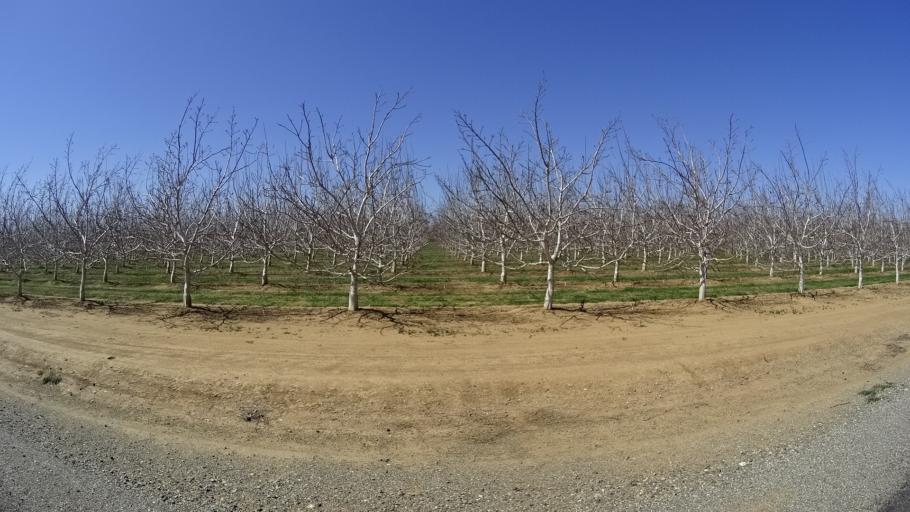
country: US
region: California
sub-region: Glenn County
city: Willows
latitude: 39.4746
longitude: -122.2490
